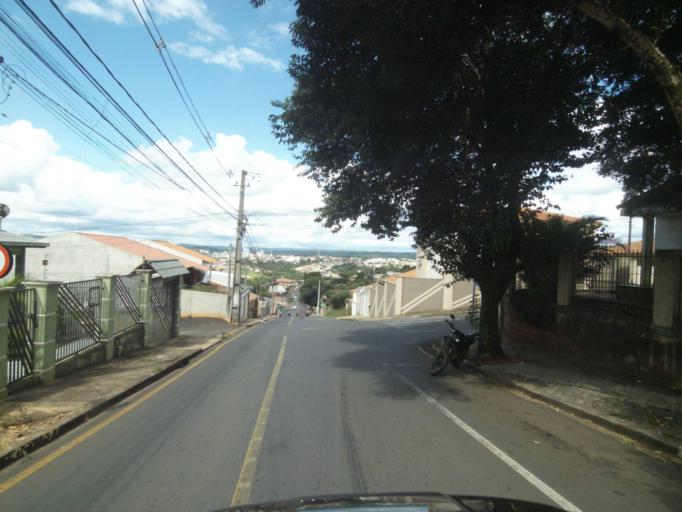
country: BR
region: Parana
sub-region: Telemaco Borba
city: Telemaco Borba
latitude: -24.3215
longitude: -50.6334
